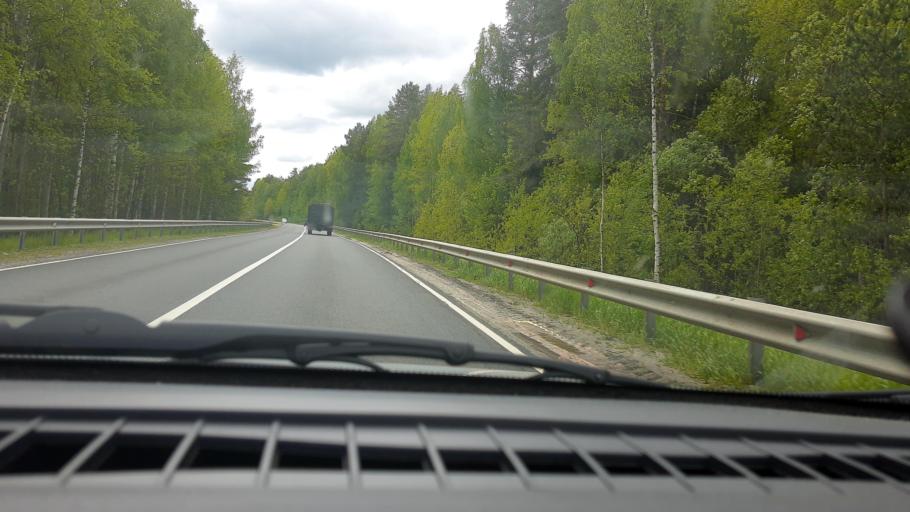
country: RU
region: Nizjnij Novgorod
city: Krasnyye Baki
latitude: 57.1323
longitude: 45.2139
